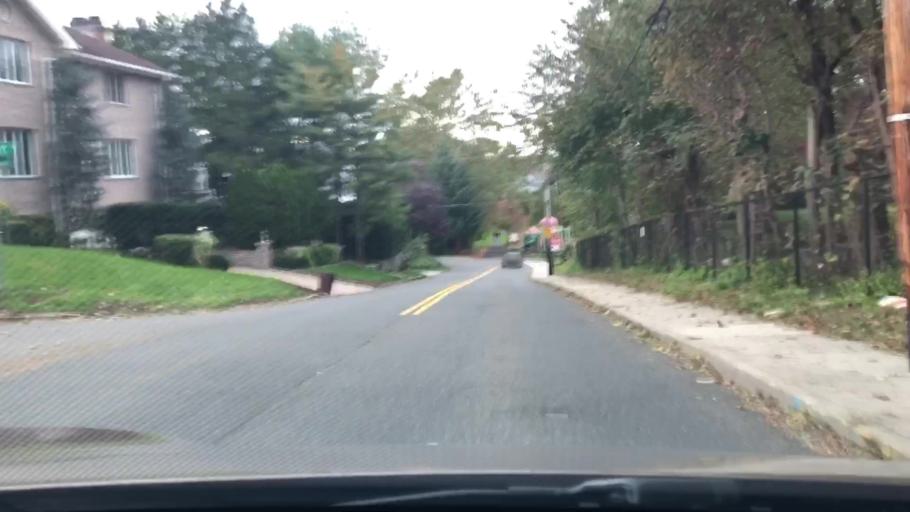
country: US
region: New York
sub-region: Westchester County
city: Tuckahoe
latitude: 40.9643
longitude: -73.8118
